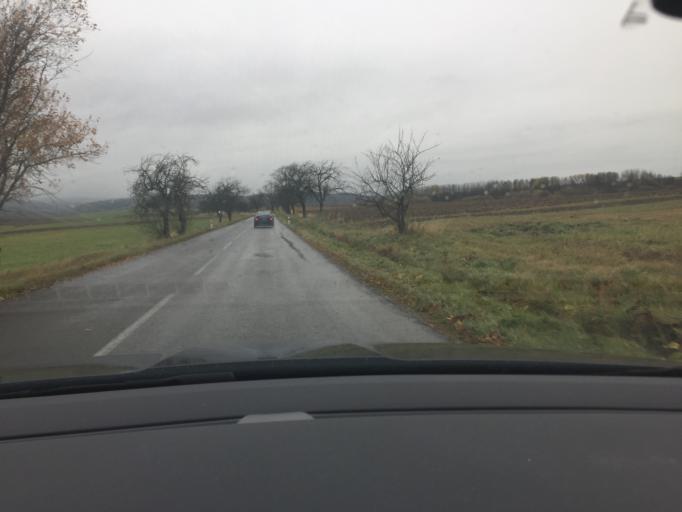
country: SK
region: Presovsky
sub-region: Okres Presov
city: Kezmarok
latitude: 49.1730
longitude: 20.4057
